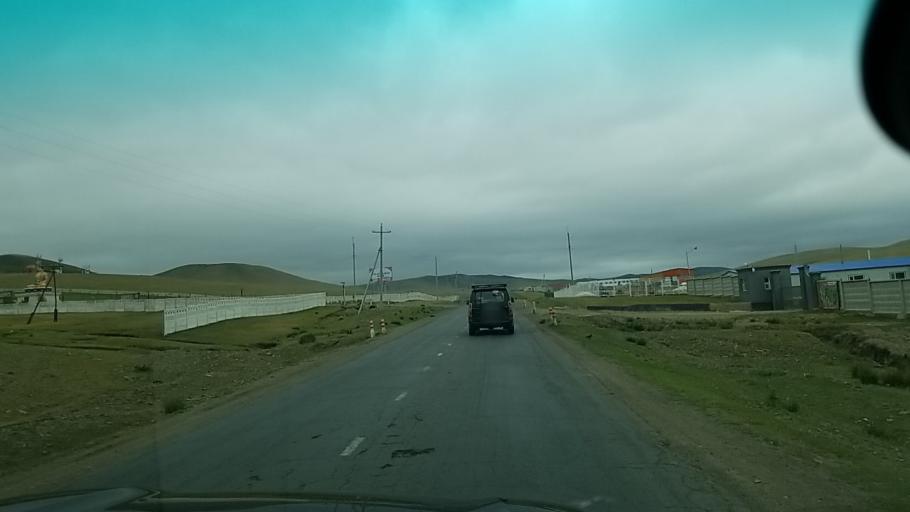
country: MN
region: Ulaanbaatar
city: Ulaanbaatar
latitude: 47.9160
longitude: 106.6292
